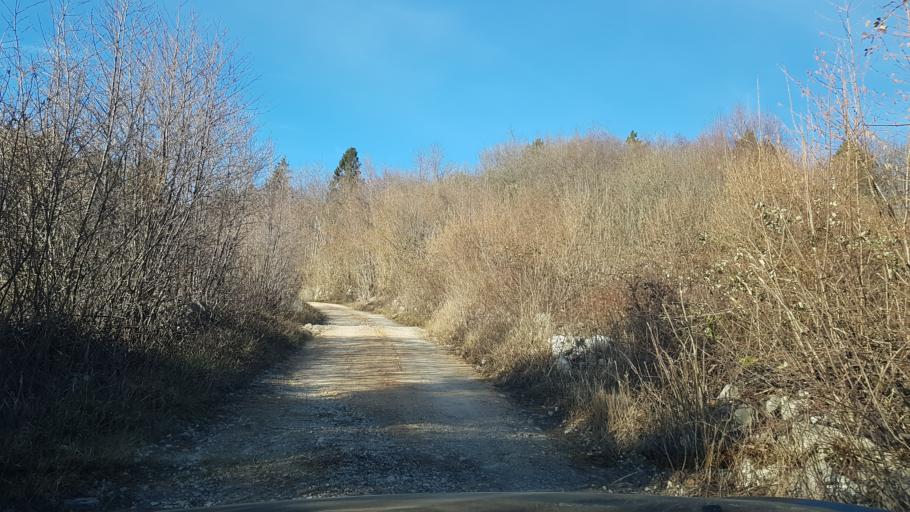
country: SI
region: Nova Gorica
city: Kromberk
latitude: 46.0153
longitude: 13.7023
